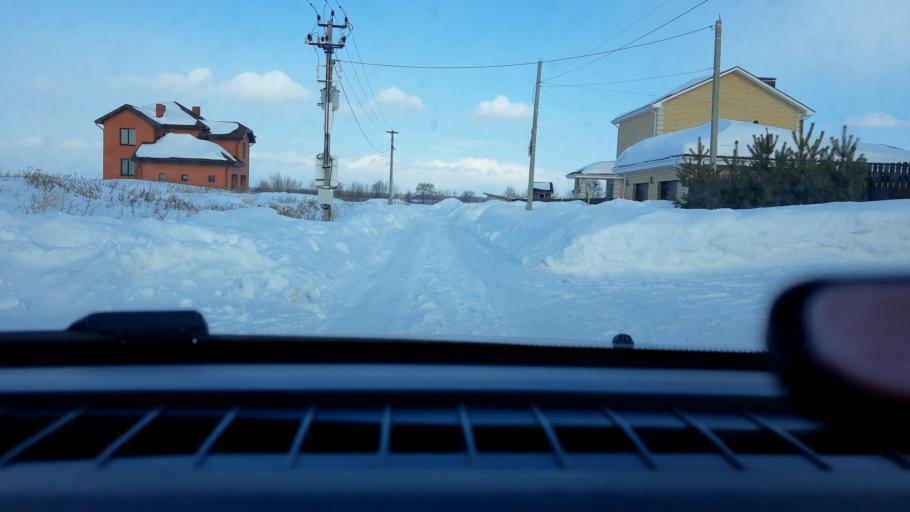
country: RU
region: Nizjnij Novgorod
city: Lukino
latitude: 56.4220
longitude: 43.7244
